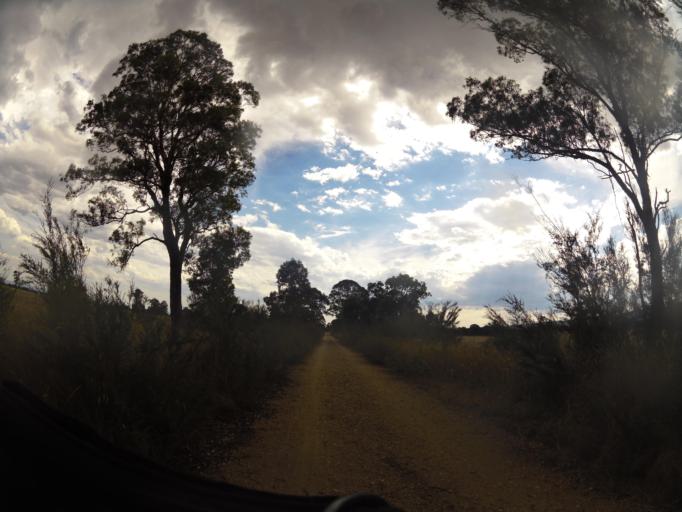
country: AU
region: Victoria
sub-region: Wellington
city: Heyfield
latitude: -38.0311
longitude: 146.6618
